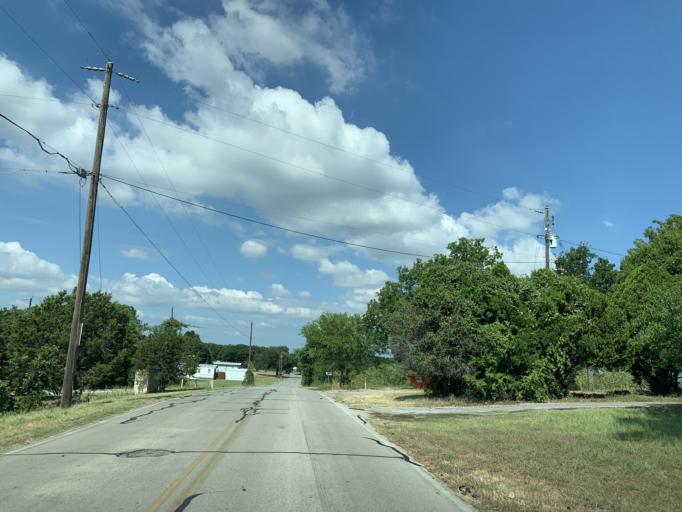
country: US
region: Texas
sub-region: Tarrant County
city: Azle
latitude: 32.8742
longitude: -97.5344
